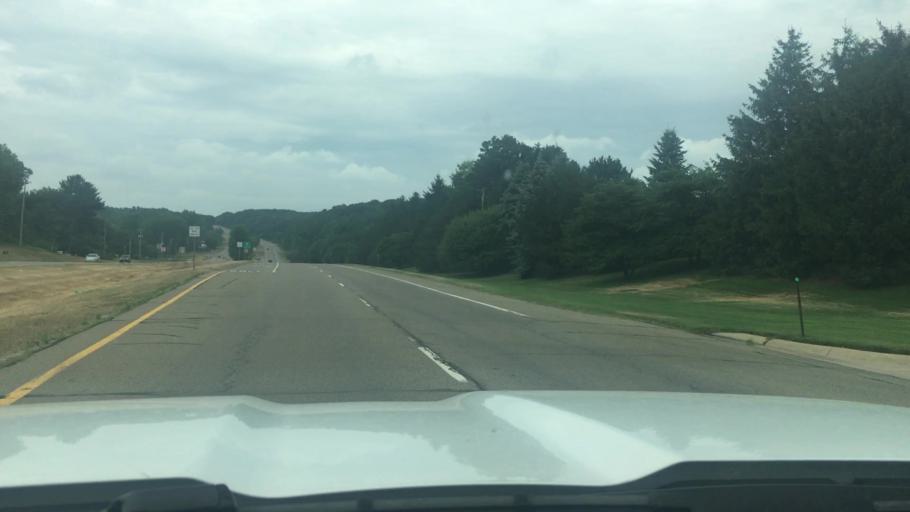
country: US
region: Michigan
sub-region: Kent County
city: Forest Hills
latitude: 42.9624
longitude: -85.5106
